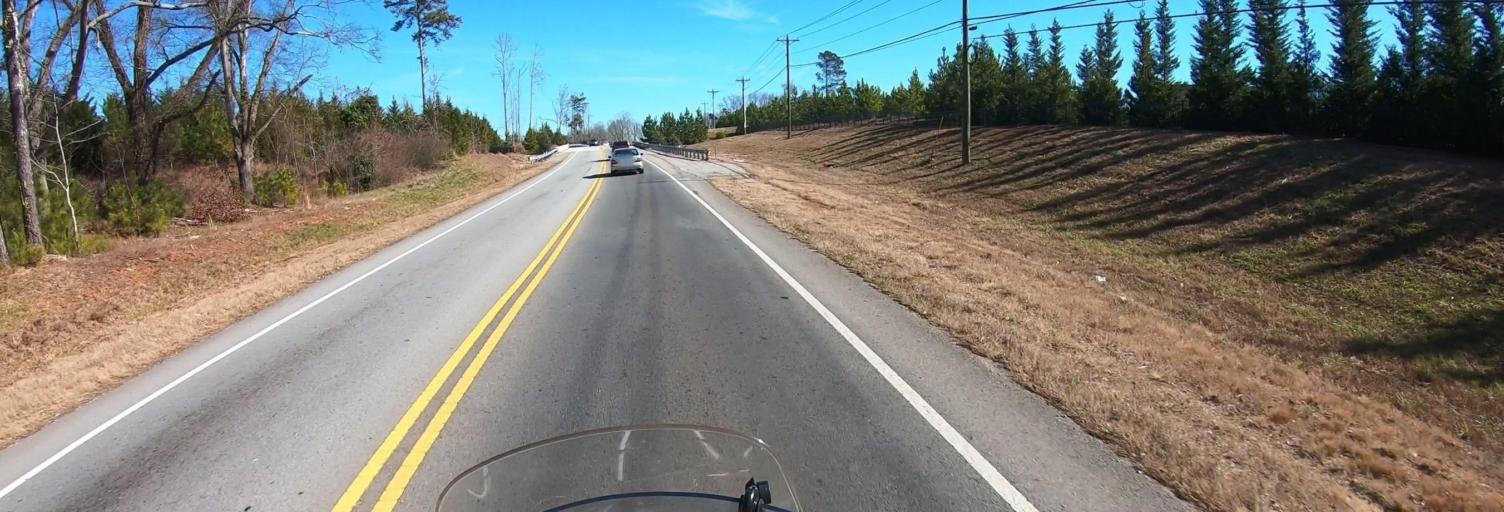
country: US
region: Georgia
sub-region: Hall County
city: Oakwood
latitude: 34.2811
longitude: -83.8961
